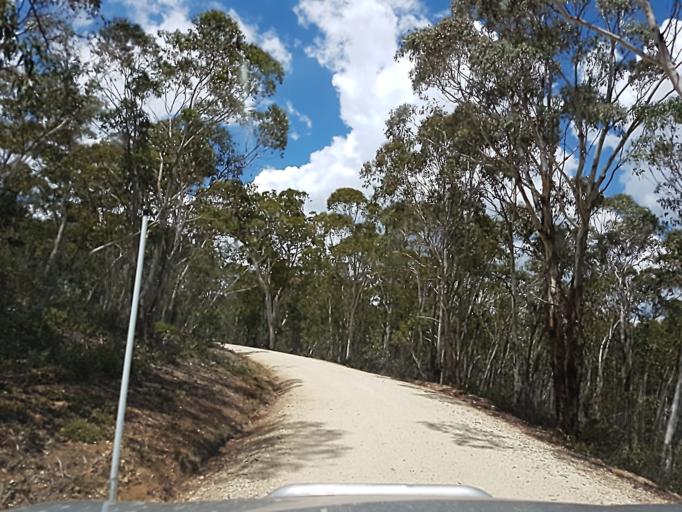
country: AU
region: New South Wales
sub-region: Snowy River
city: Jindabyne
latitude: -36.9005
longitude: 148.0944
